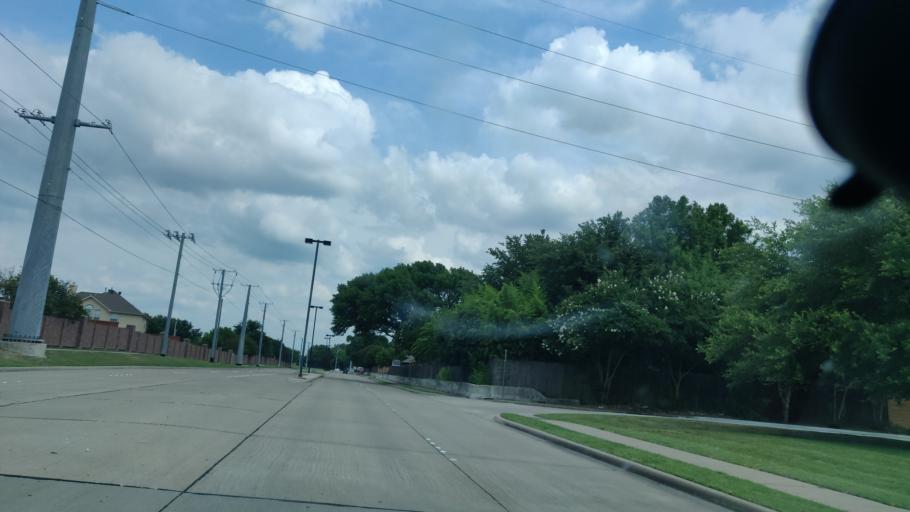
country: US
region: Texas
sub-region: Dallas County
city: Garland
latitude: 32.9384
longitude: -96.6099
